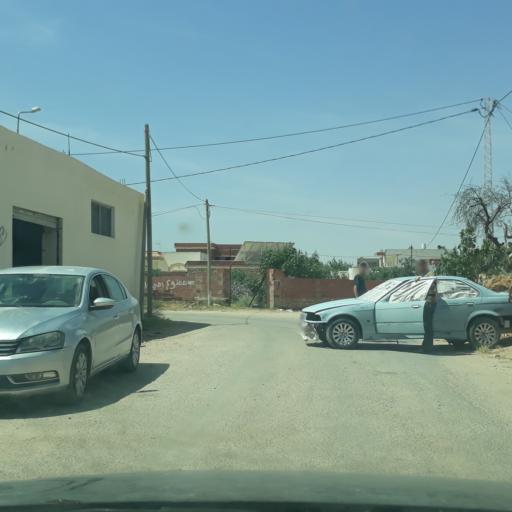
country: TN
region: Safaqis
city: Al Qarmadah
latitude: 34.8277
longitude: 10.7793
